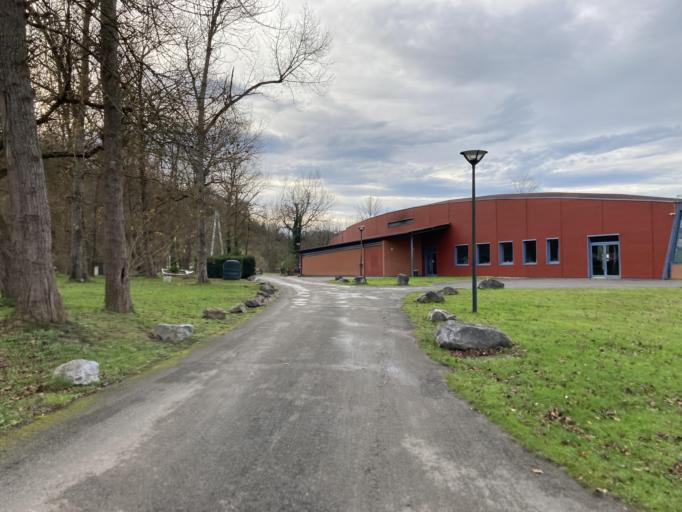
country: FR
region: Aquitaine
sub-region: Departement des Pyrenees-Atlantiques
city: Lescar
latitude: 43.3066
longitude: -0.4340
